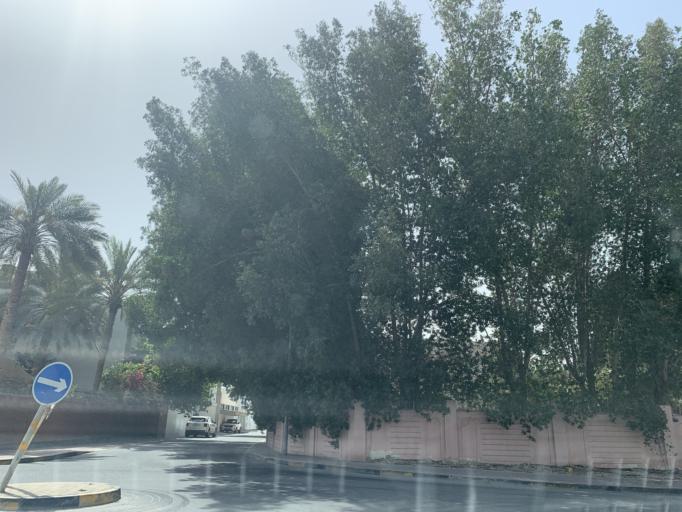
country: BH
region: Manama
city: Jidd Hafs
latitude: 26.2203
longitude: 50.5593
